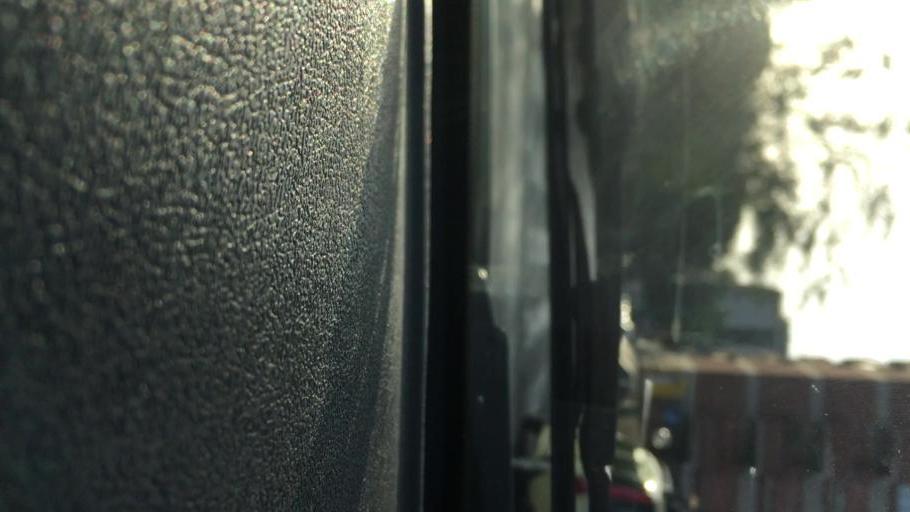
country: IT
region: Latium
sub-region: Citta metropolitana di Roma Capitale
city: Rome
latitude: 41.8379
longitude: 12.4841
